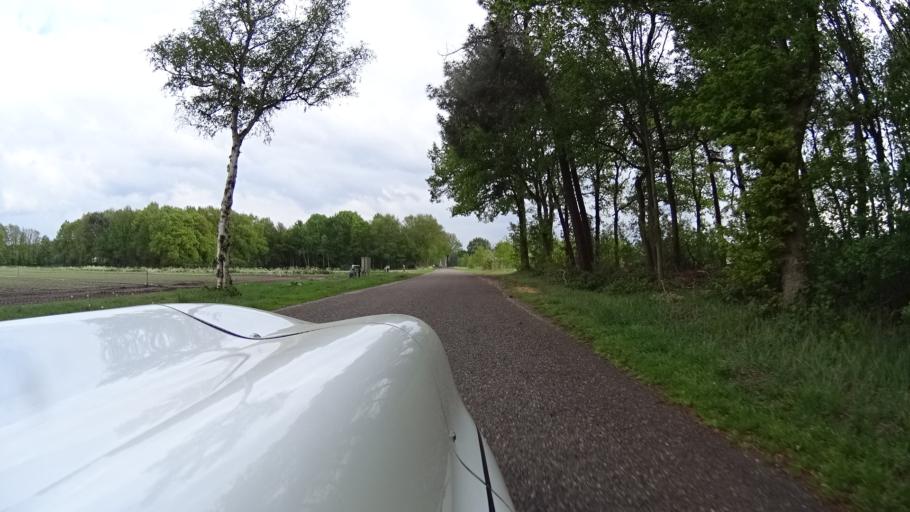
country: NL
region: North Brabant
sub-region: Gemeente Uden
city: Odiliapeel
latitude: 51.6302
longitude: 5.6861
